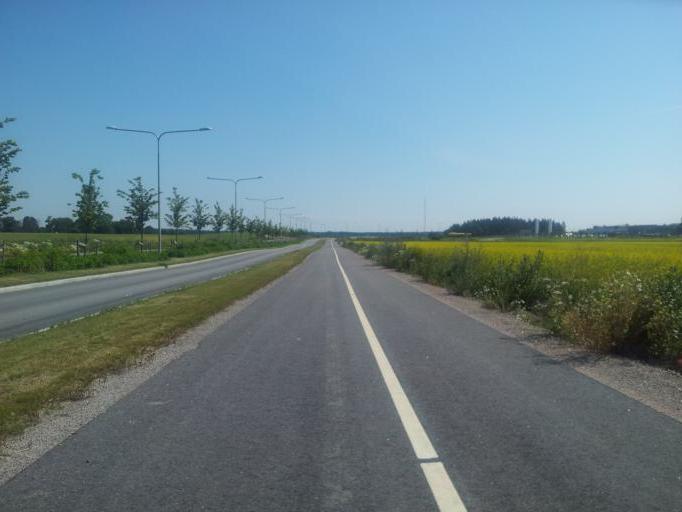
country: SE
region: Uppsala
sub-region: Uppsala Kommun
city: Saevja
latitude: 59.8539
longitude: 17.7121
